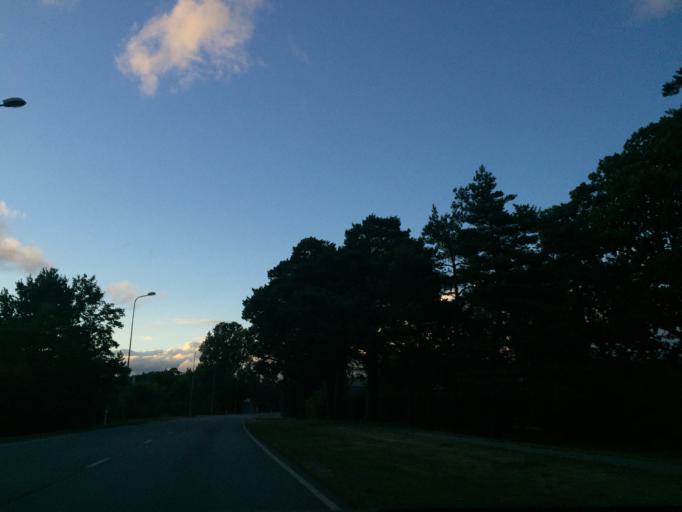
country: LV
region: Saulkrastu
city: Saulkrasti
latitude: 57.3035
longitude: 24.4095
